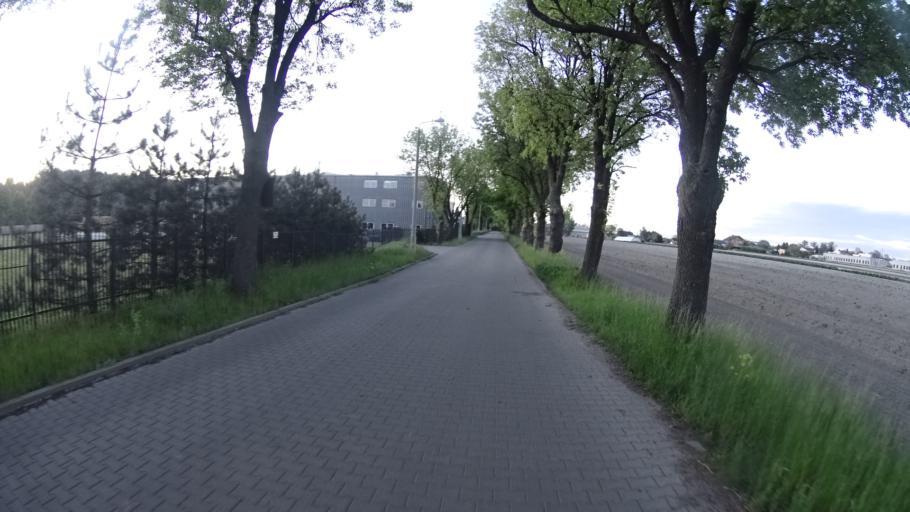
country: PL
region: Masovian Voivodeship
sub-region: Powiat warszawski zachodni
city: Ozarow Mazowiecki
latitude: 52.2082
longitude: 20.7554
